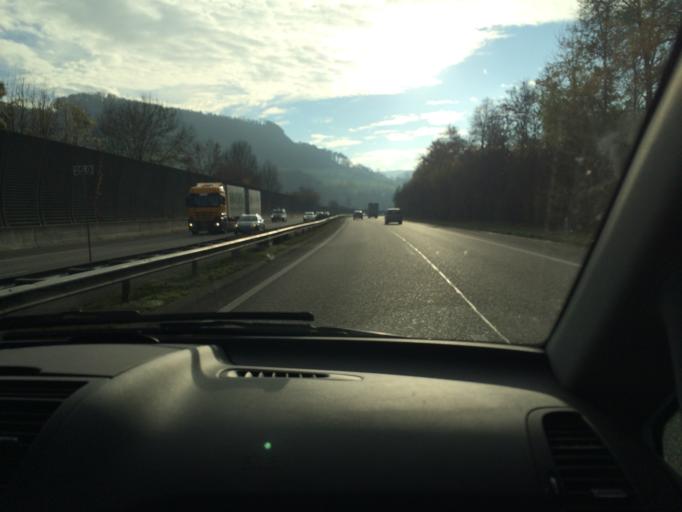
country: CH
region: Basel-Landschaft
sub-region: Bezirk Sissach
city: Zunzgen
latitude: 47.4487
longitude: 7.8039
